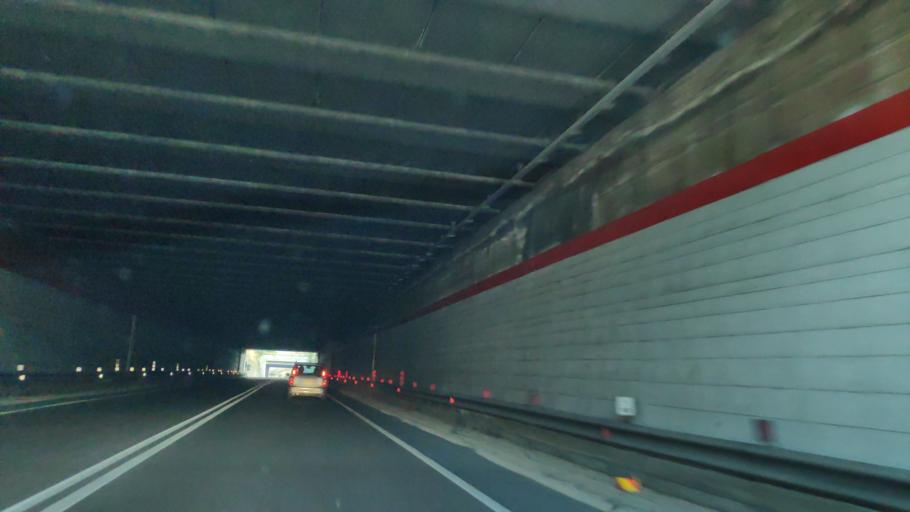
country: IT
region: Calabria
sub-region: Provincia di Catanzaro
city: Soverato Superiore
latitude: 38.6940
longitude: 16.5390
